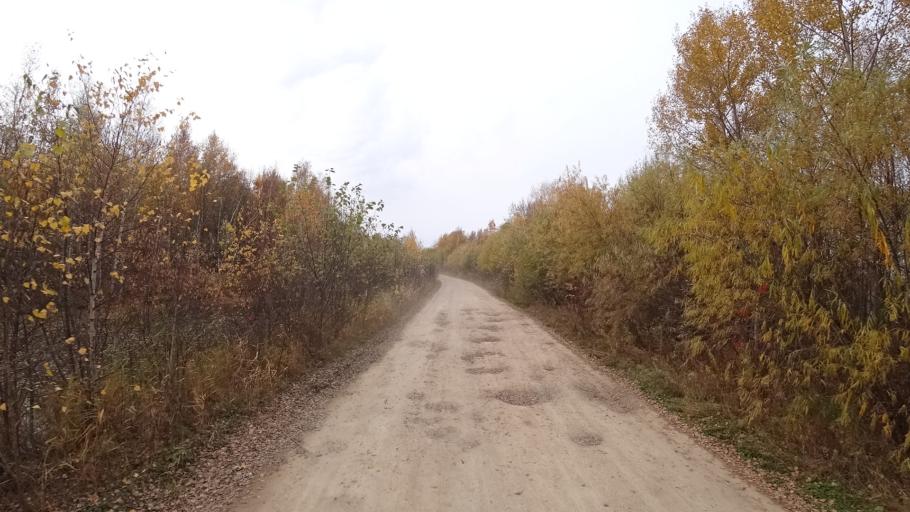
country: RU
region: Khabarovsk Krai
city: Amursk
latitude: 50.1471
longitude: 136.9747
